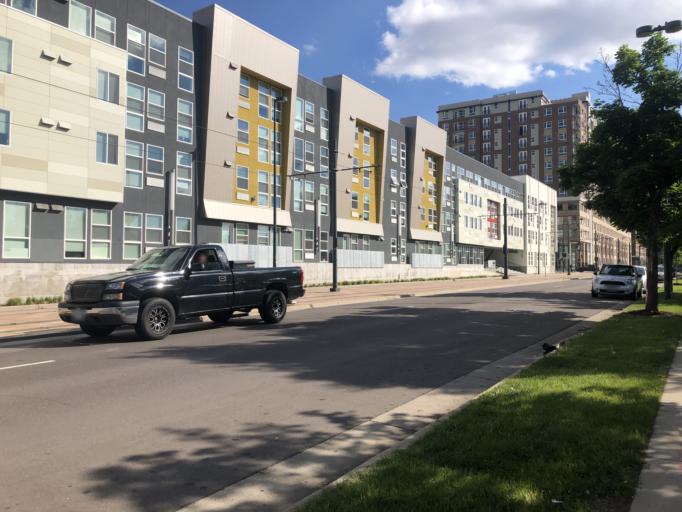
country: US
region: Colorado
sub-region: Denver County
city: Denver
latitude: 39.7519
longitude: -104.9816
